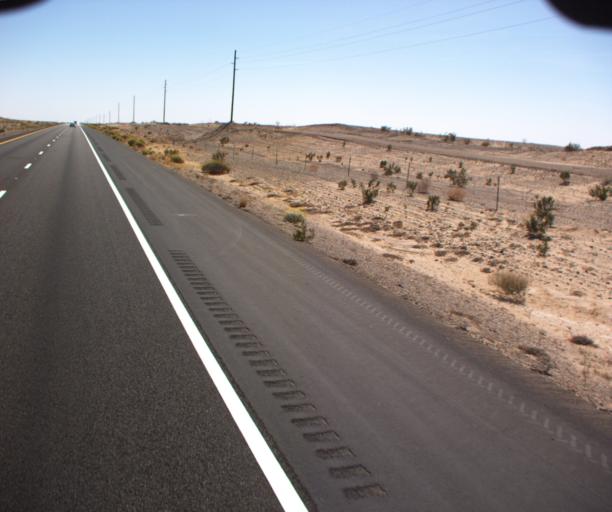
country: US
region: Arizona
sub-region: Yuma County
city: Somerton
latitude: 32.5405
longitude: -114.5623
